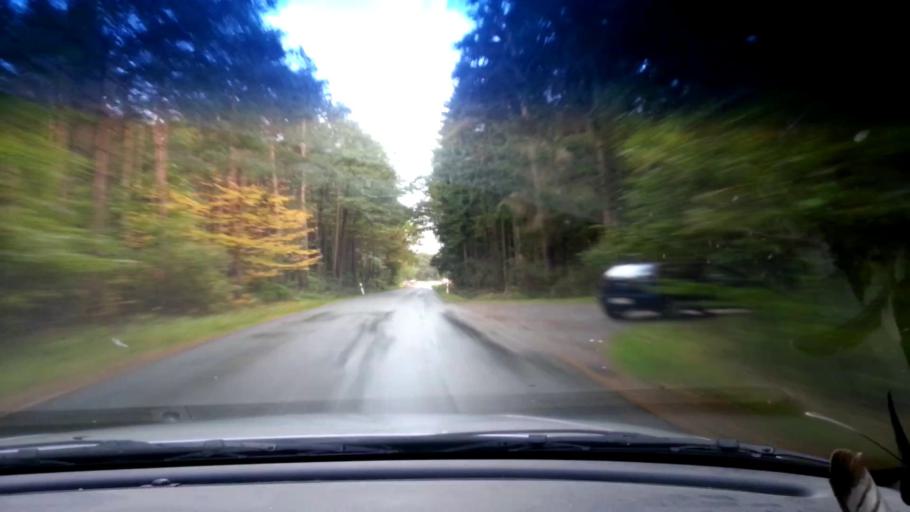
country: DE
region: Bavaria
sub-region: Upper Franconia
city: Burgebrach
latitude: 49.8003
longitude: 10.7095
